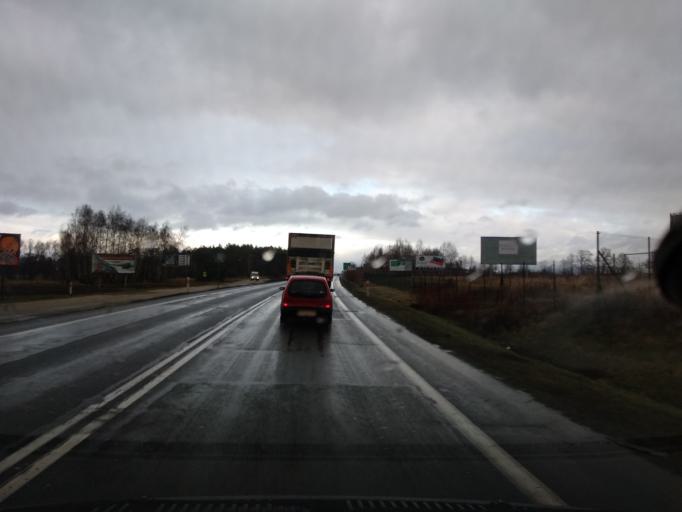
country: PL
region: Greater Poland Voivodeship
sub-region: Powiat koninski
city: Stare Miasto
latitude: 52.1671
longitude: 18.2091
